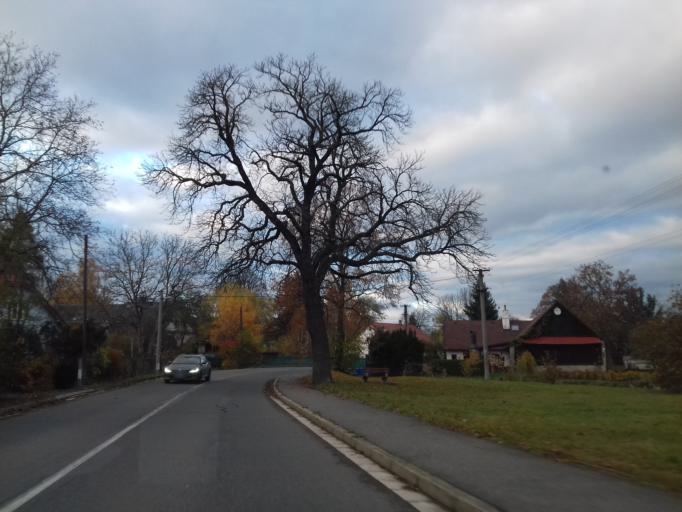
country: CZ
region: Pardubicky
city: Krouna
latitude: 49.7743
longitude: 16.0263
